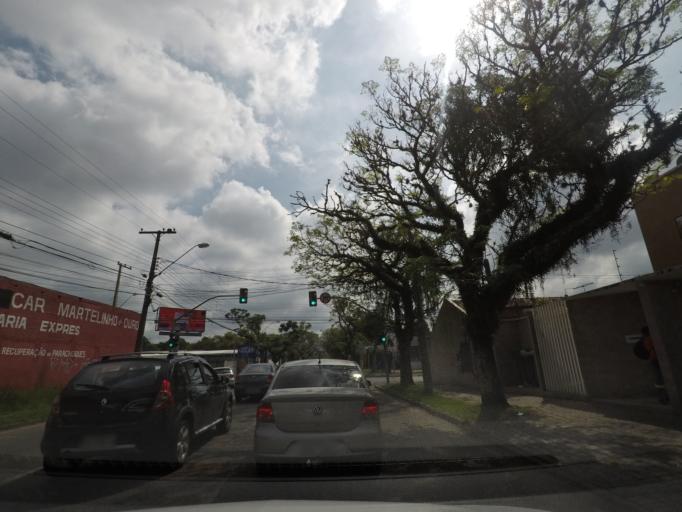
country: BR
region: Parana
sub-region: Curitiba
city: Curitiba
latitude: -25.4473
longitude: -49.2562
